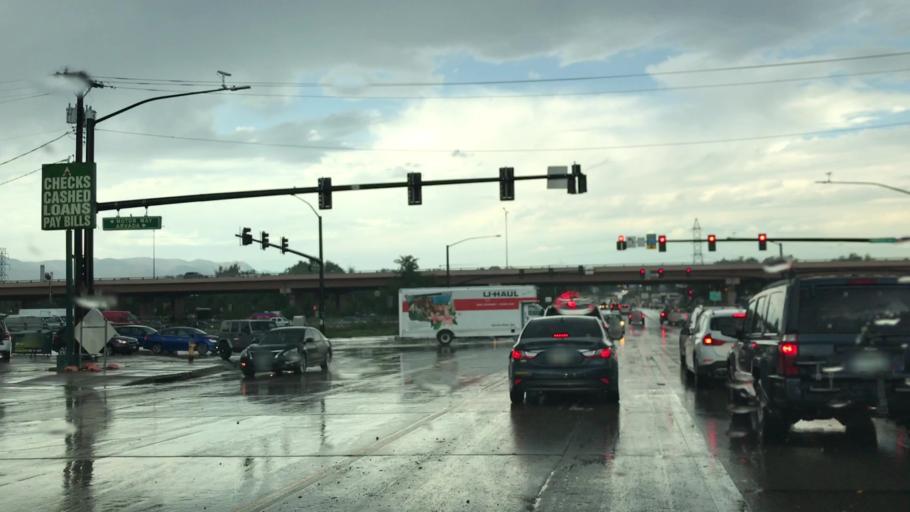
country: US
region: Colorado
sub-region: El Paso County
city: Colorado Springs
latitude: 38.8135
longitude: -104.8223
